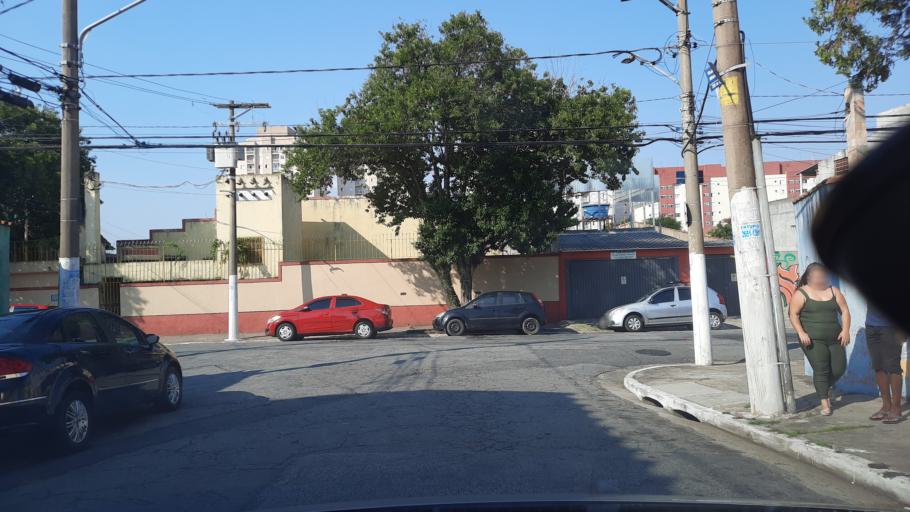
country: BR
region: Sao Paulo
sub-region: Guarulhos
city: Guarulhos
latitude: -23.5441
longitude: -46.5116
